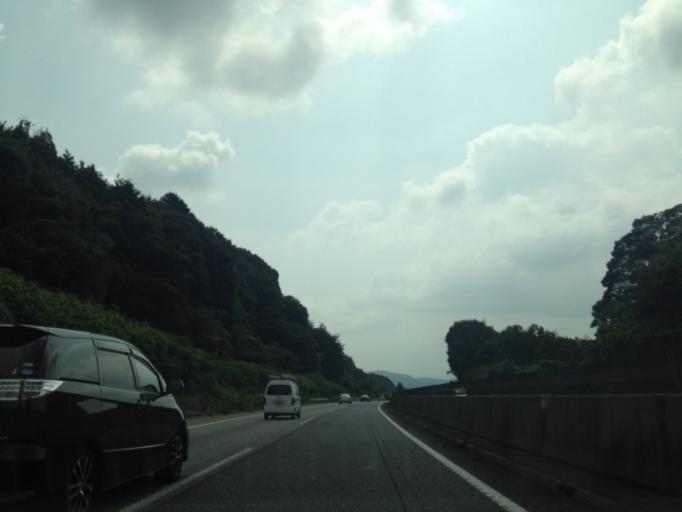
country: JP
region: Aichi
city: Gamagori
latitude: 34.8755
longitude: 137.2810
